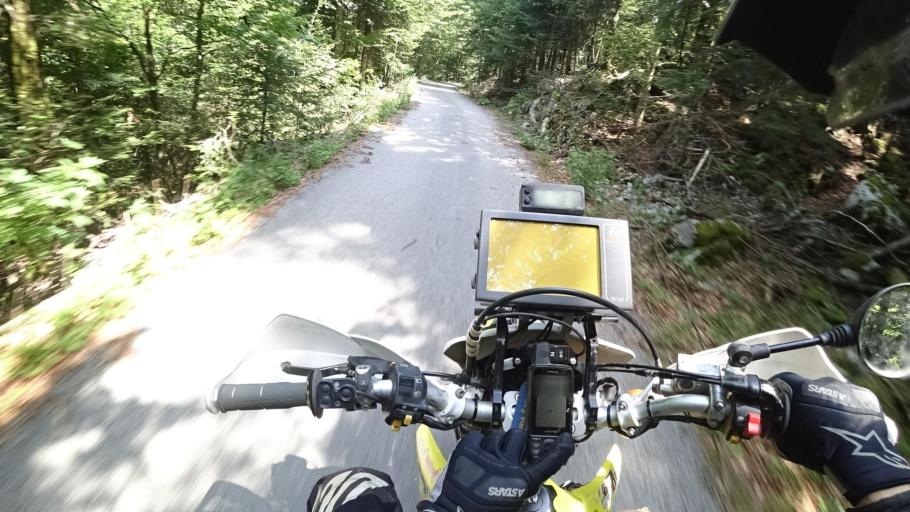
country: HR
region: Primorsko-Goranska
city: Bribir
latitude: 45.2271
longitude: 14.8548
